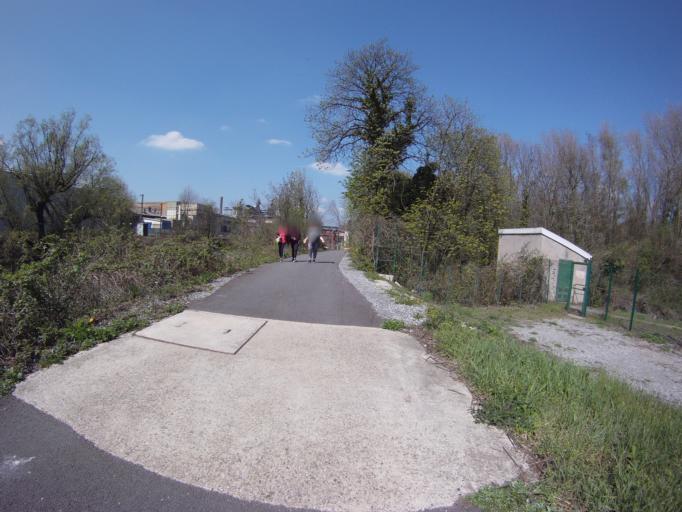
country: FR
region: Lorraine
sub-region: Departement de Meurthe-et-Moselle
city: Blenod-les-Pont-a-Mousson
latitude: 48.8903
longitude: 6.0576
